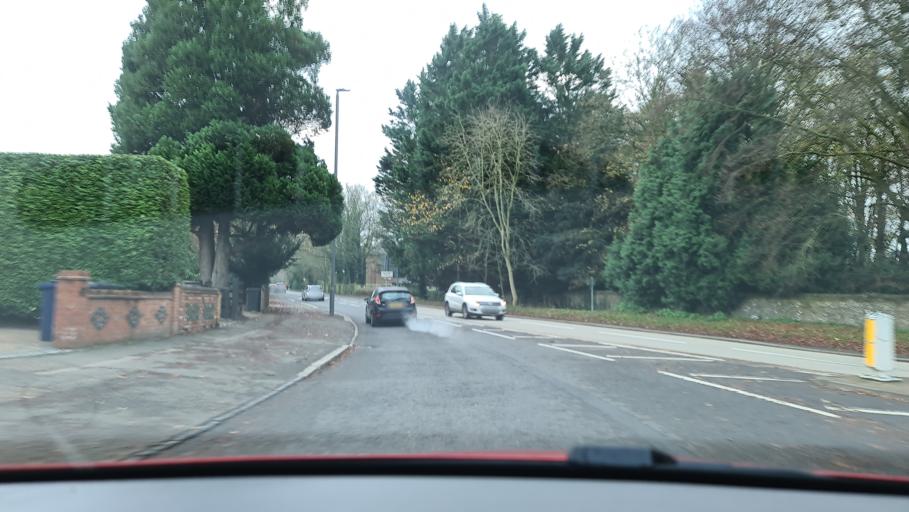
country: GB
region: England
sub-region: Buckinghamshire
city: High Wycombe
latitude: 51.6446
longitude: -0.7961
